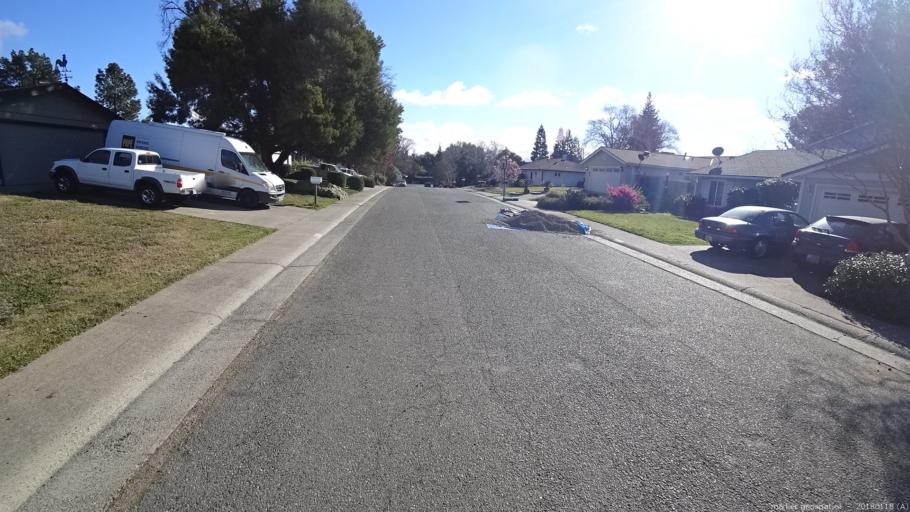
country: US
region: California
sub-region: Sacramento County
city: Orangevale
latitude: 38.6755
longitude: -121.2367
